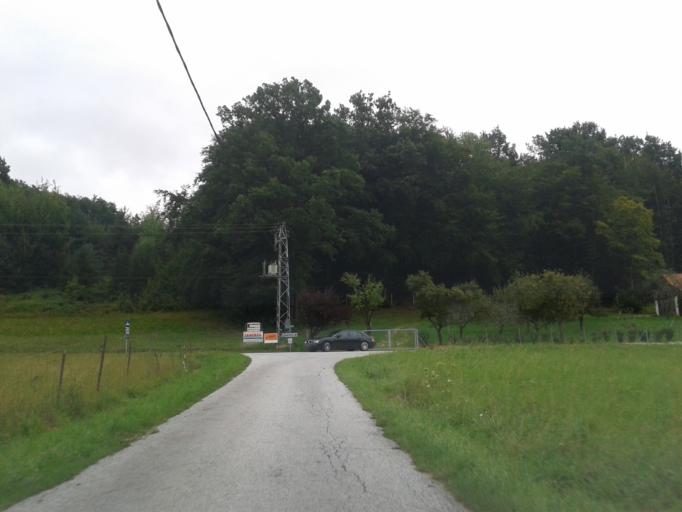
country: AT
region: Styria
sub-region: Politischer Bezirk Weiz
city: Sankt Ruprecht an der Raab
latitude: 47.1267
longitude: 15.6536
